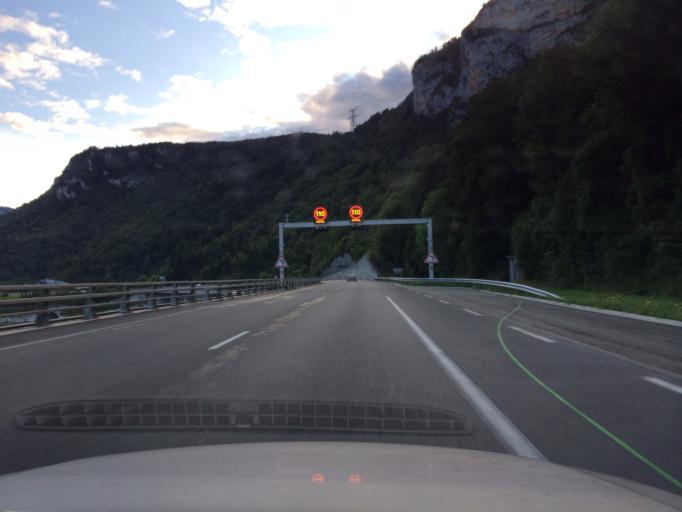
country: FR
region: Rhone-Alpes
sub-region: Departement de l'Ain
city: Nantua
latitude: 46.1623
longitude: 5.6577
